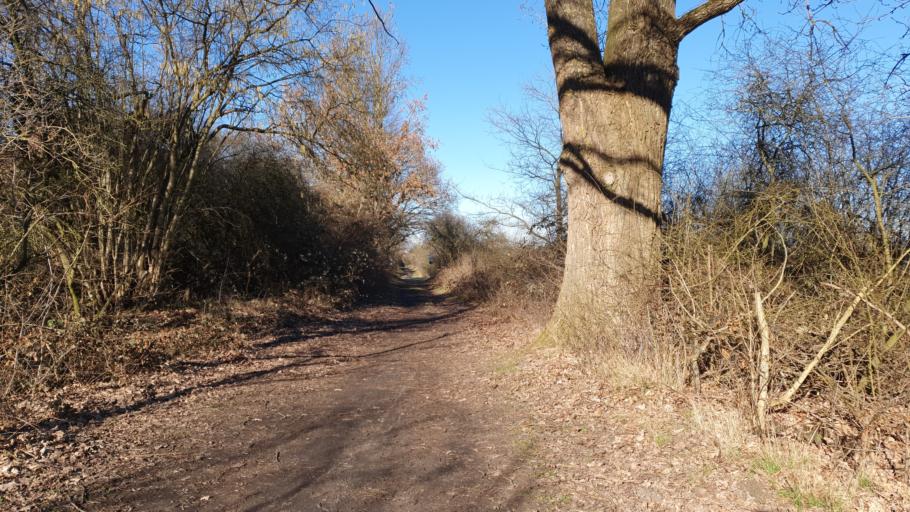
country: DE
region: Mecklenburg-Vorpommern
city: Neumuehle
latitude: 53.6382
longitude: 11.3609
